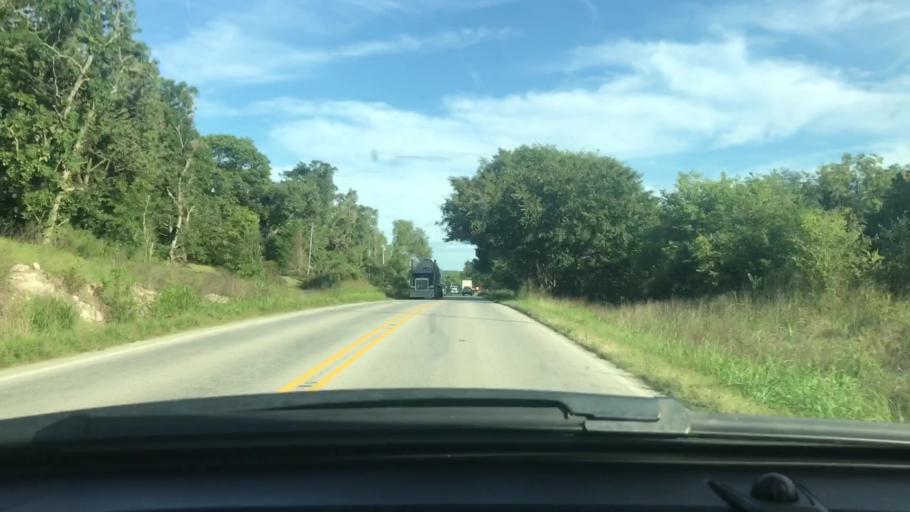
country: US
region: Arkansas
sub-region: Sharp County
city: Cherokee Village
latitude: 36.3068
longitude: -91.4540
